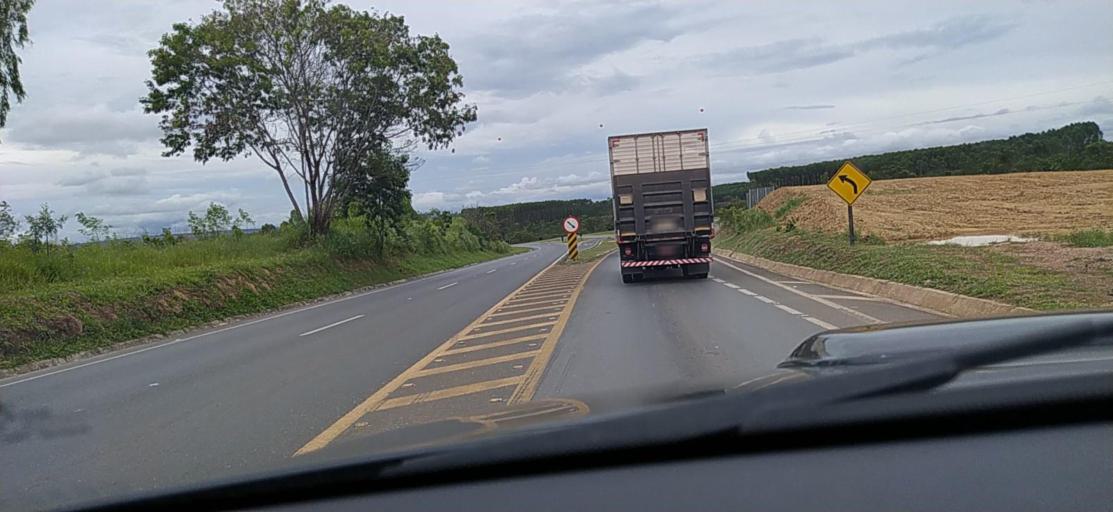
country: BR
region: Minas Gerais
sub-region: Curvelo
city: Curvelo
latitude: -18.7069
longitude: -44.4412
